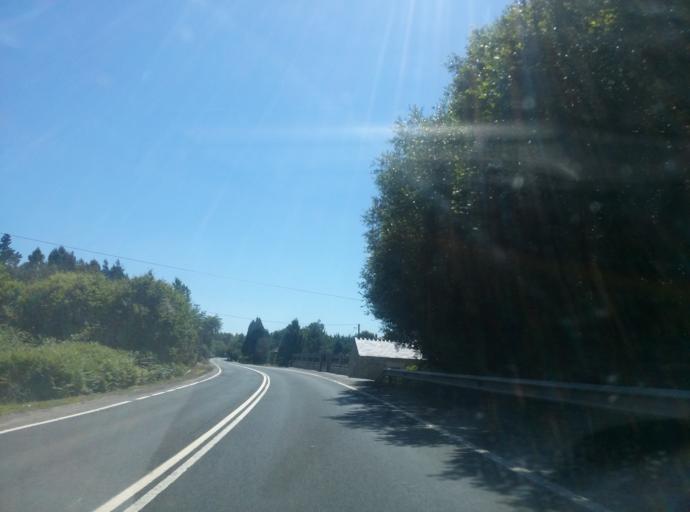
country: ES
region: Galicia
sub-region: Provincia de Lugo
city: Castro de Rei
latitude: 43.1556
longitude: -7.3881
